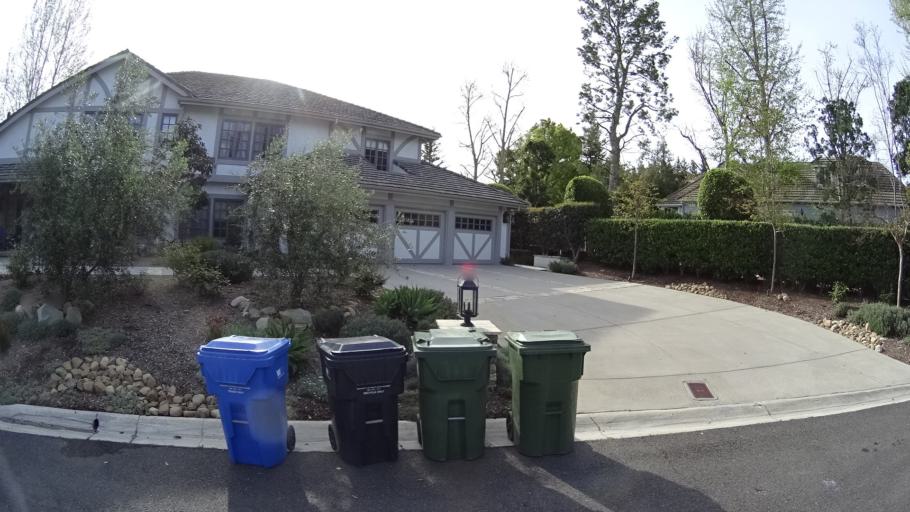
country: US
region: California
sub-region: Ventura County
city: Thousand Oaks
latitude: 34.1897
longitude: -118.8065
